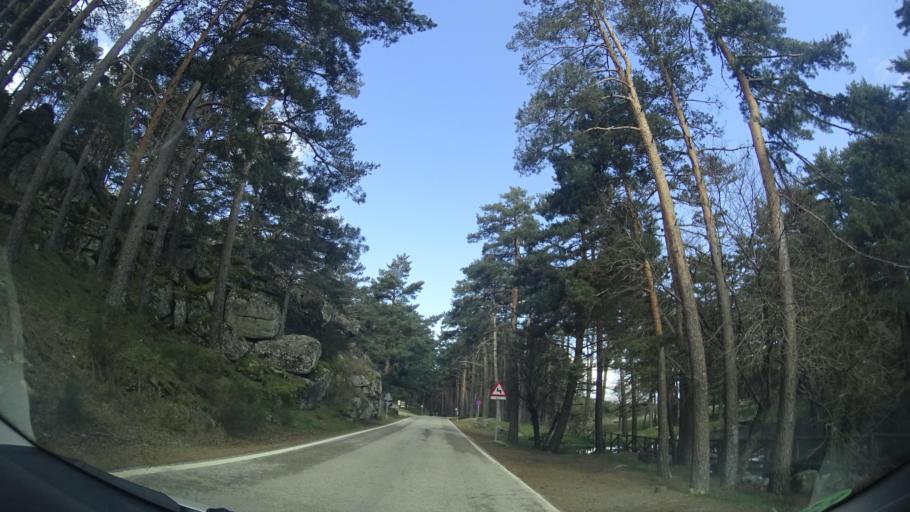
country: ES
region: Madrid
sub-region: Provincia de Madrid
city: Canencia
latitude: 40.8690
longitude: -3.7640
